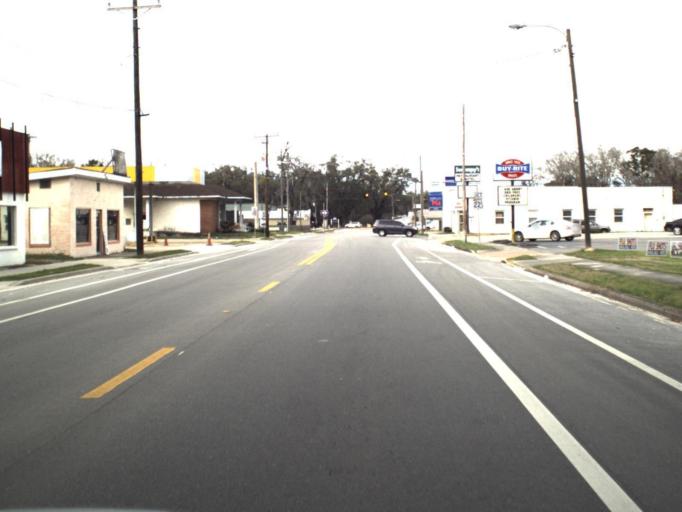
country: US
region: Florida
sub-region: Gulf County
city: Wewahitchka
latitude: 30.1114
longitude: -85.2003
